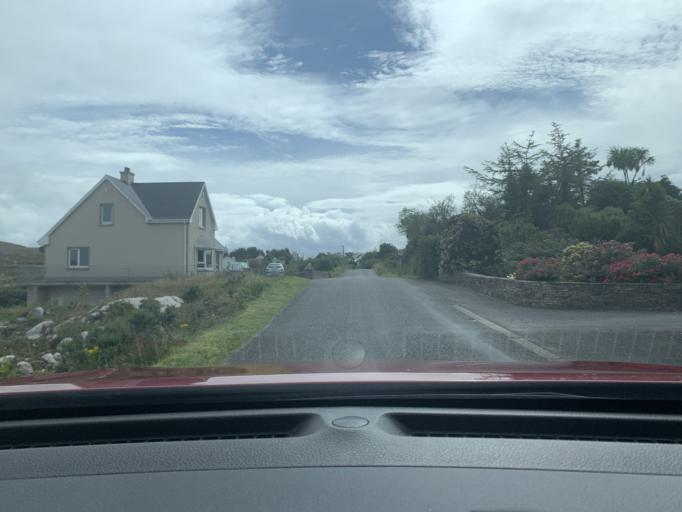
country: IE
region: Ulster
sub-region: County Donegal
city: Dungloe
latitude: 54.9427
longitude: -8.3585
